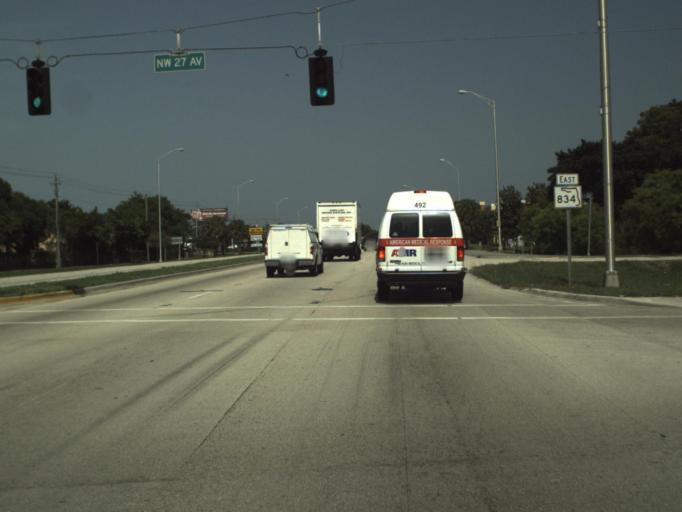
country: US
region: Florida
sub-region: Broward County
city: Coconut Creek
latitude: 26.2743
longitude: -80.1602
